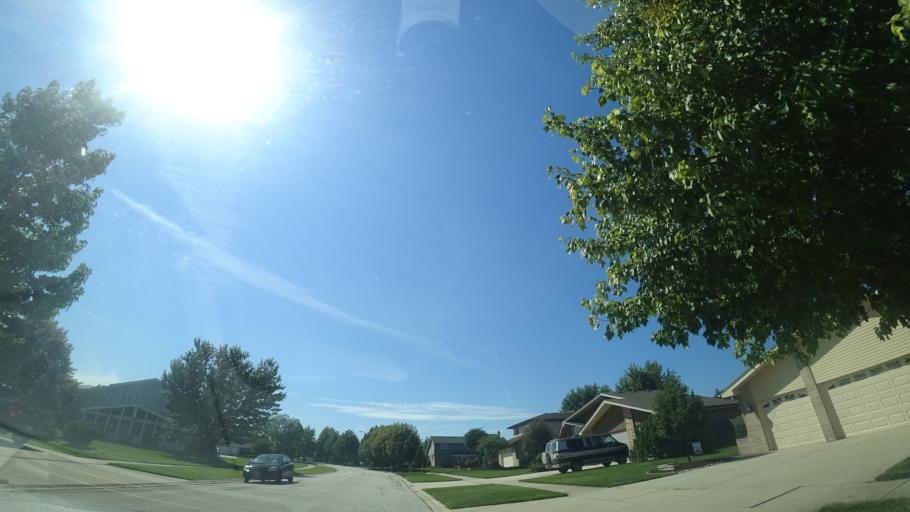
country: US
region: Illinois
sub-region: Will County
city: Homer Glen
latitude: 41.5721
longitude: -87.9013
